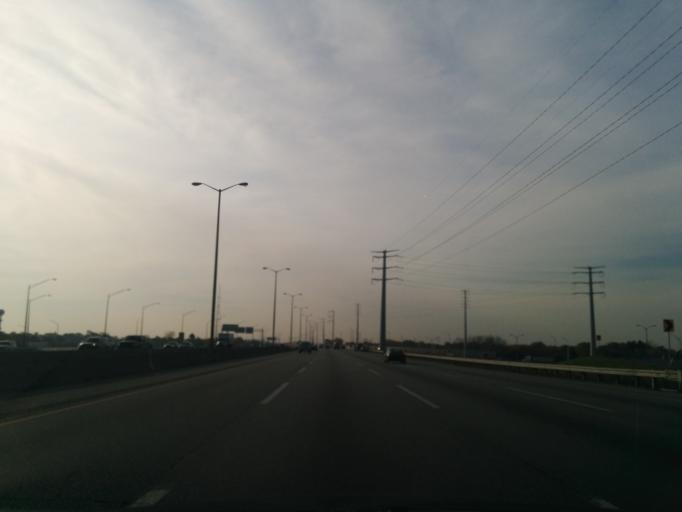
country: US
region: Illinois
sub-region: Cook County
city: Hillside
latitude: 41.8816
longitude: -87.9195
